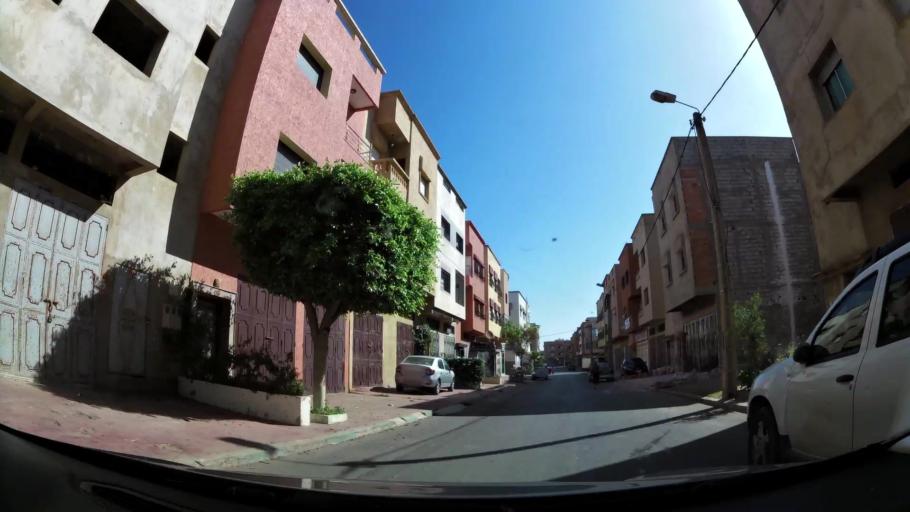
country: MA
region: Rabat-Sale-Zemmour-Zaer
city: Sale
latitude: 34.0725
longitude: -6.7982
